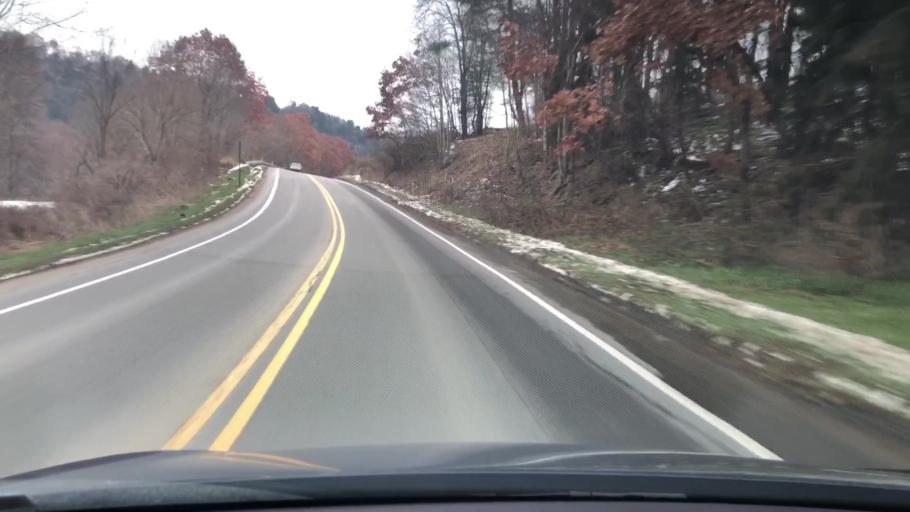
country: US
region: Pennsylvania
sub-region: Clarion County
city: Clarion
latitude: 41.0155
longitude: -79.2782
